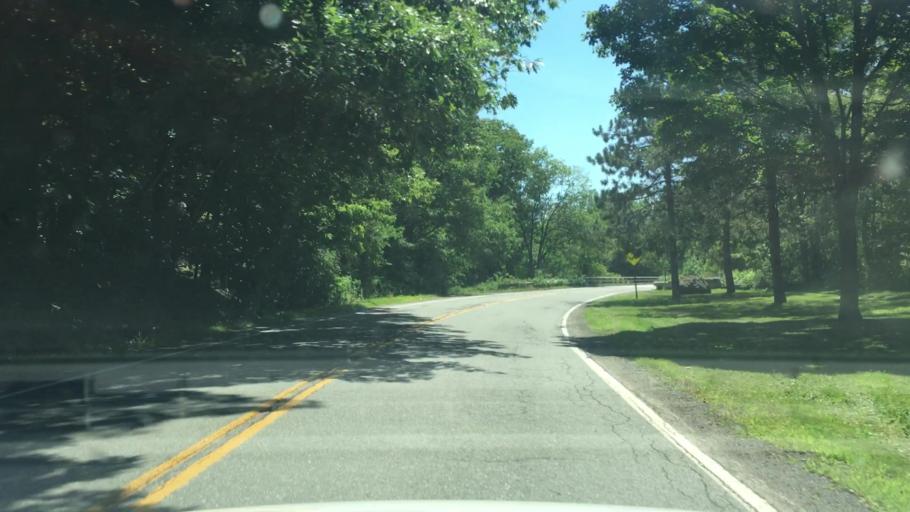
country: US
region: Maine
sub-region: Penobscot County
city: Bangor
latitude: 44.8139
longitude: -68.7845
